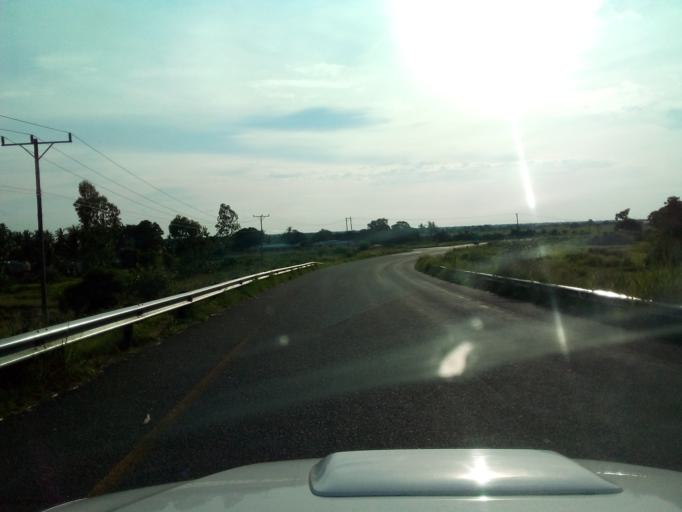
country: MZ
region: Zambezia
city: Quelimane
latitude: -17.4944
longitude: 37.0221
